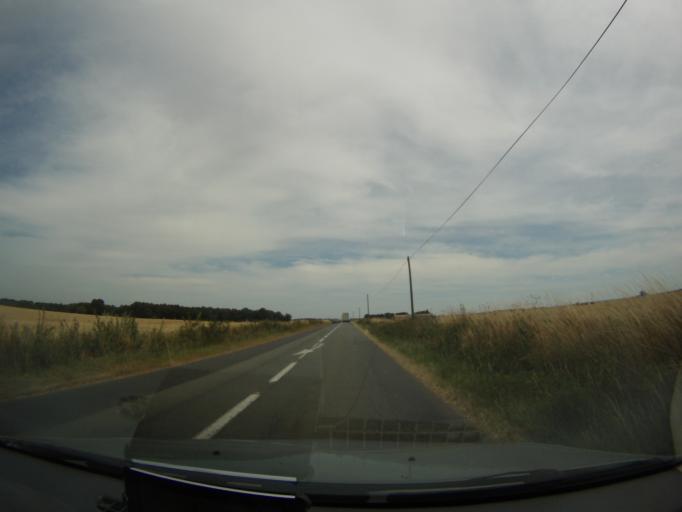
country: FR
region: Poitou-Charentes
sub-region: Departement de la Vienne
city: Mirebeau
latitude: 46.7441
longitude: 0.1788
